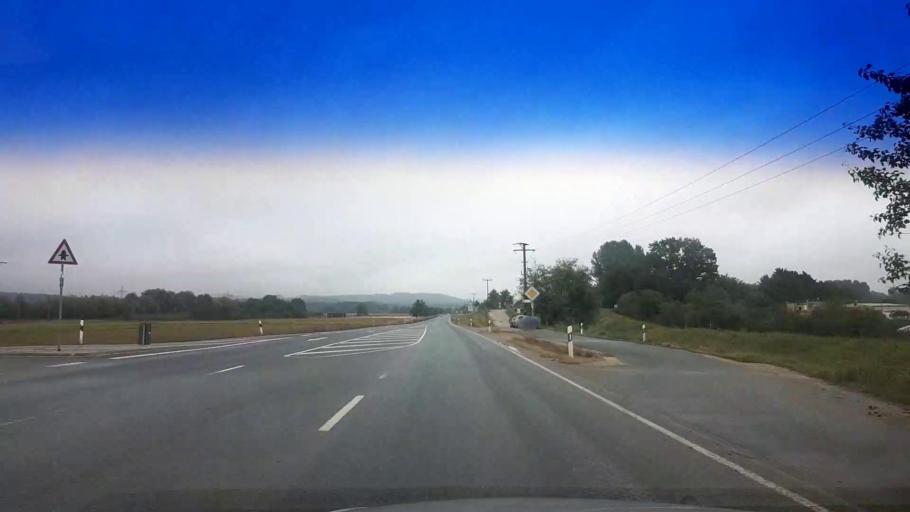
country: DE
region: Bavaria
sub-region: Upper Franconia
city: Eggolsheim
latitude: 49.7630
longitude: 11.0448
